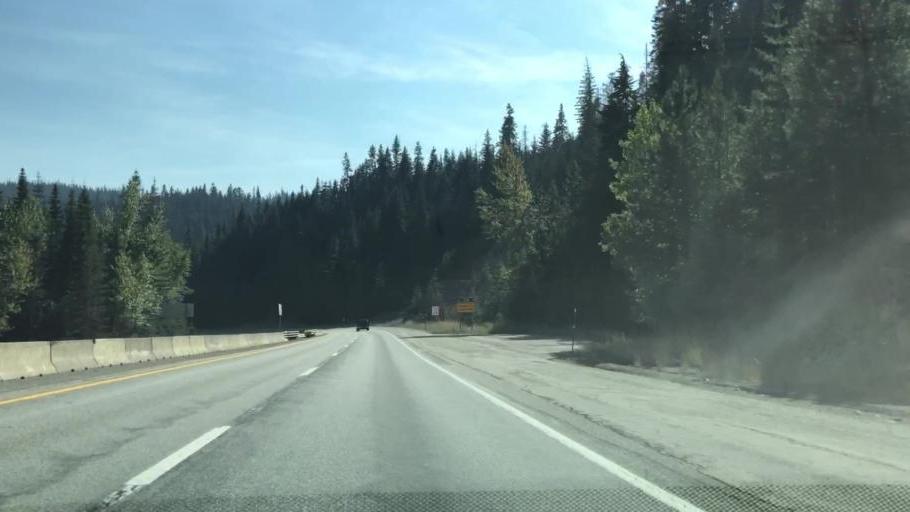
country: US
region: Idaho
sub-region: Kootenai County
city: Coeur d'Alene
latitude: 47.6161
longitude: -116.5209
